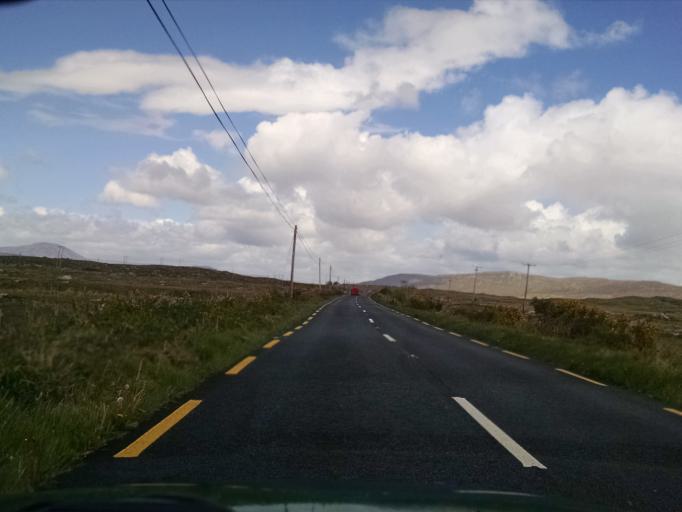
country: IE
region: Connaught
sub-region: County Galway
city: Oughterard
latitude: 53.3447
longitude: -9.5446
